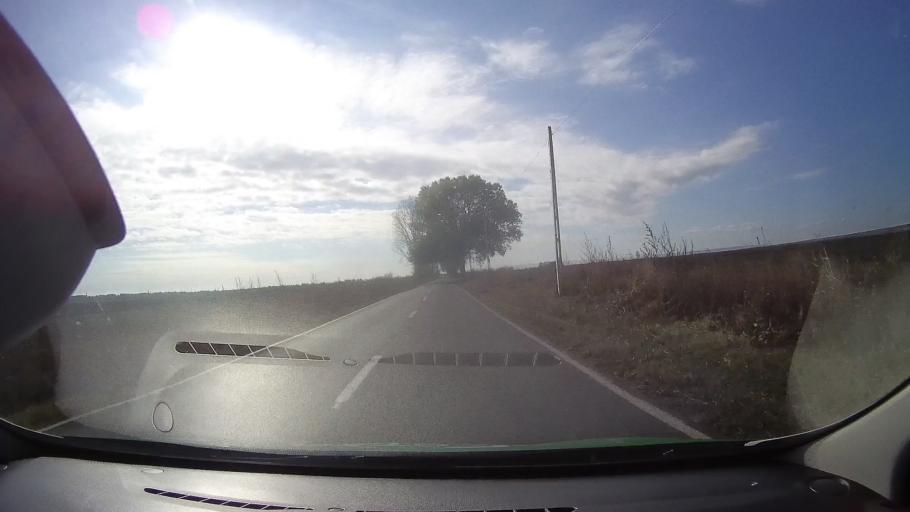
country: RO
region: Tulcea
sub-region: Comuna Valea Nucarilor
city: Agighiol
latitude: 44.9912
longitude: 28.8856
